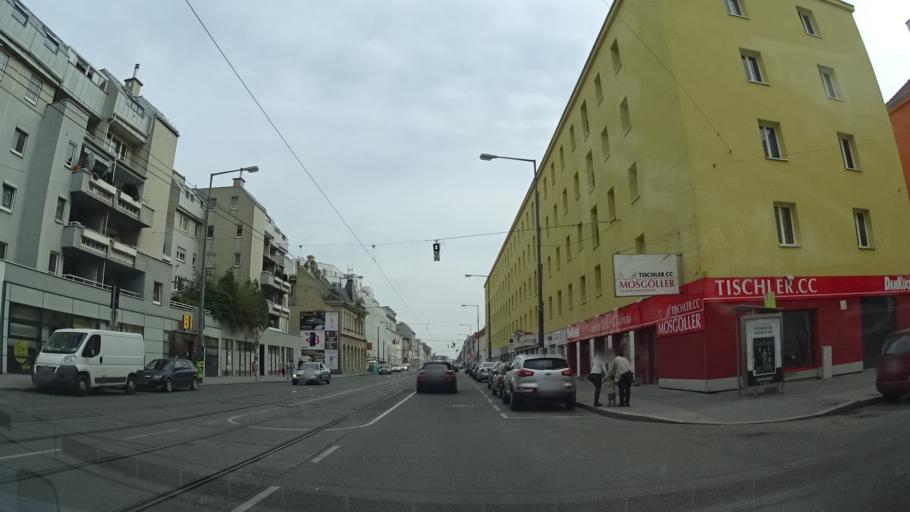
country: AT
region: Lower Austria
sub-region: Politischer Bezirk Korneuburg
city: Langenzersdorf
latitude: 48.2702
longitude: 16.3913
